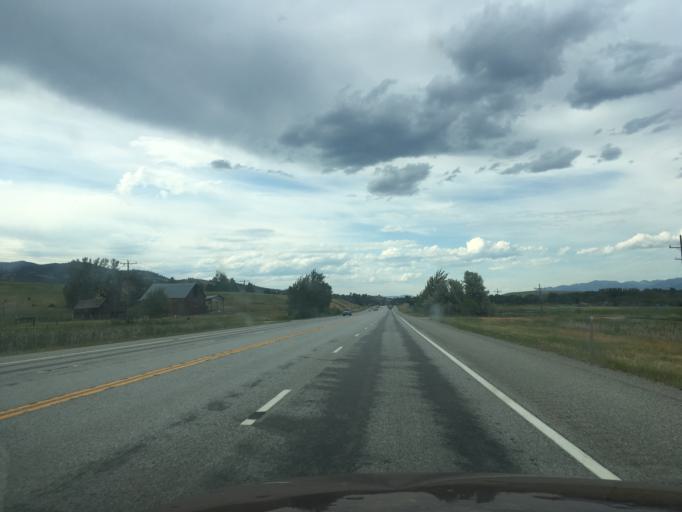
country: US
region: Montana
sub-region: Missoula County
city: Lolo
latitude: 46.7349
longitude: -114.0802
